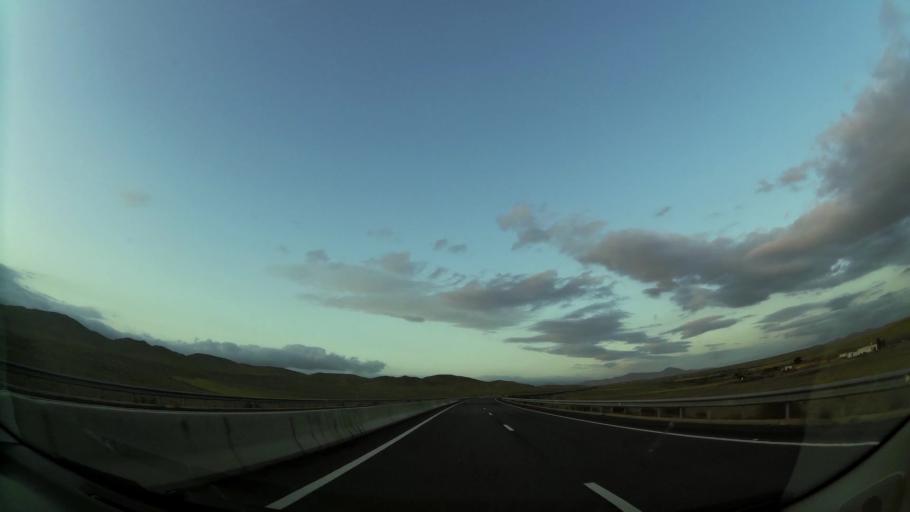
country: MA
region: Oriental
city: Taourirt
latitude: 34.5832
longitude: -2.8047
